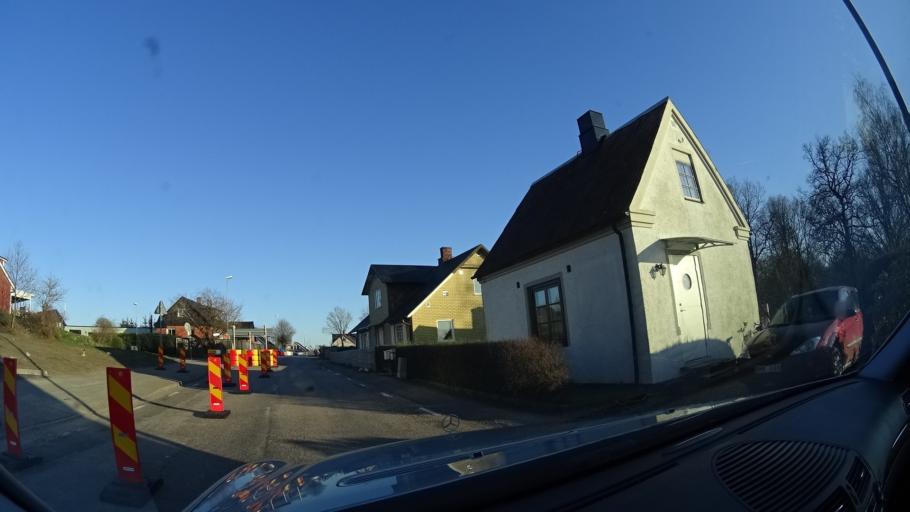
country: SE
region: Skane
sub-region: Bjuvs Kommun
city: Billesholm
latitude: 56.0565
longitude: 12.9943
